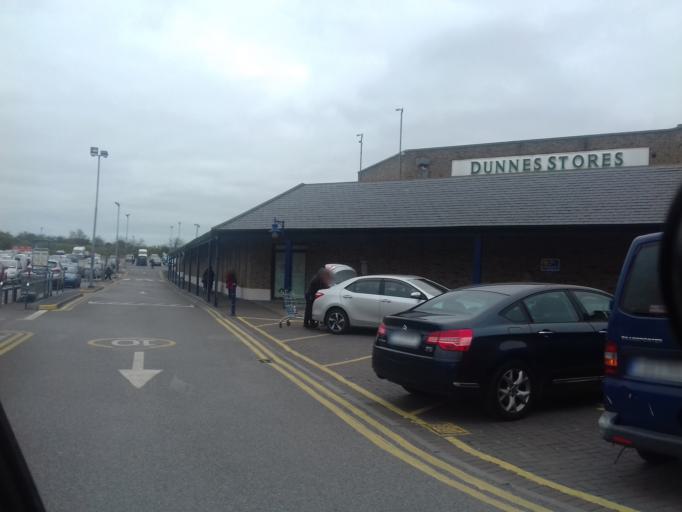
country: IE
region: Leinster
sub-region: An Iarmhi
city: An Muileann gCearr
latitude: 53.5286
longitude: -7.3406
